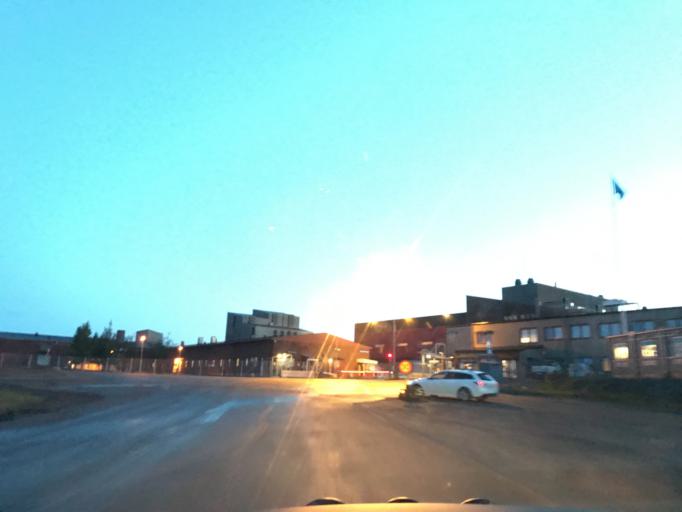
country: SE
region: Norrbotten
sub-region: Gallivare Kommun
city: Malmberget
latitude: 67.6392
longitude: 21.0152
